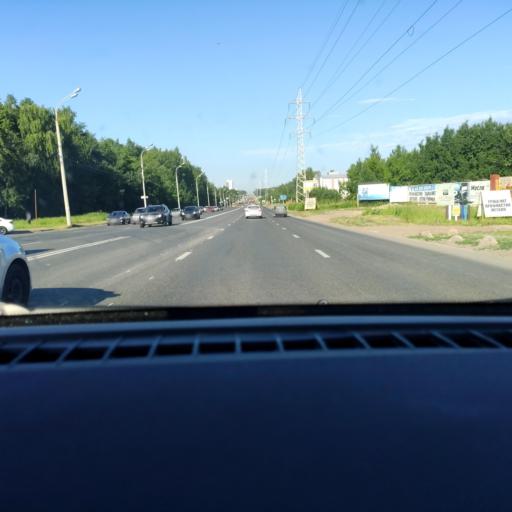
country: RU
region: Udmurtiya
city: Khokhryaki
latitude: 56.8989
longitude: 53.3066
